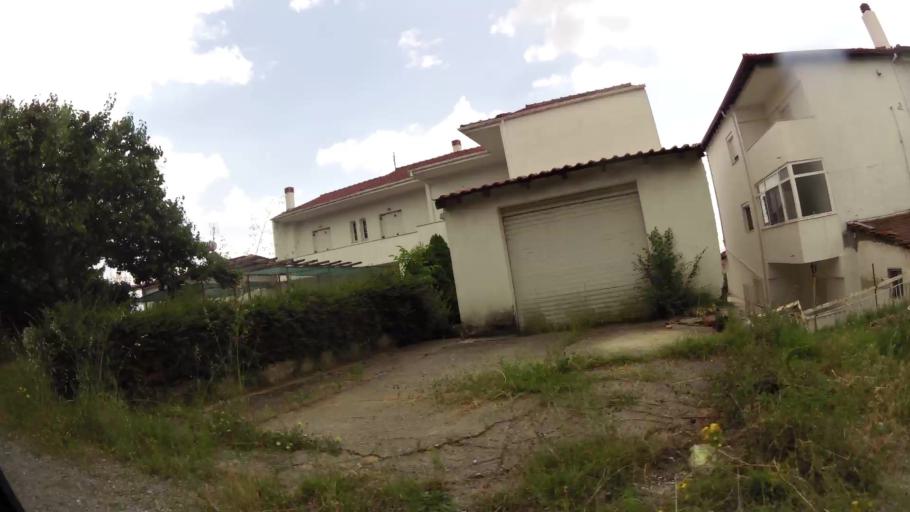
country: GR
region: West Macedonia
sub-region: Nomos Kozanis
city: Koila
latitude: 40.3230
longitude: 21.8239
